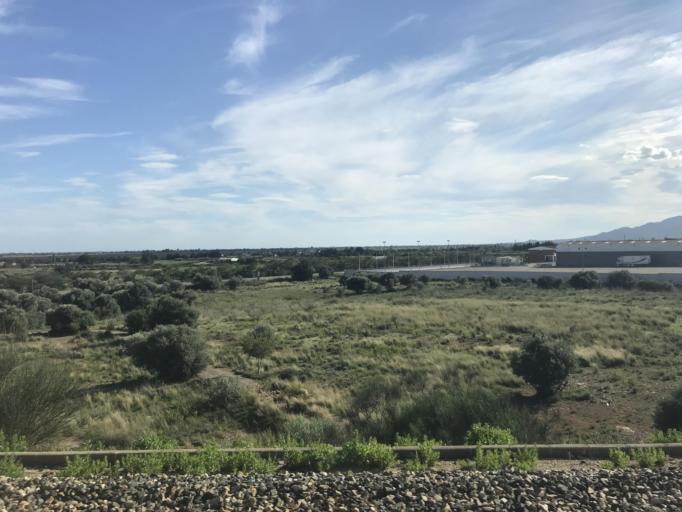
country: ES
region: Catalonia
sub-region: Provincia de Tarragona
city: Camarles
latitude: 40.7594
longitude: 0.6358
